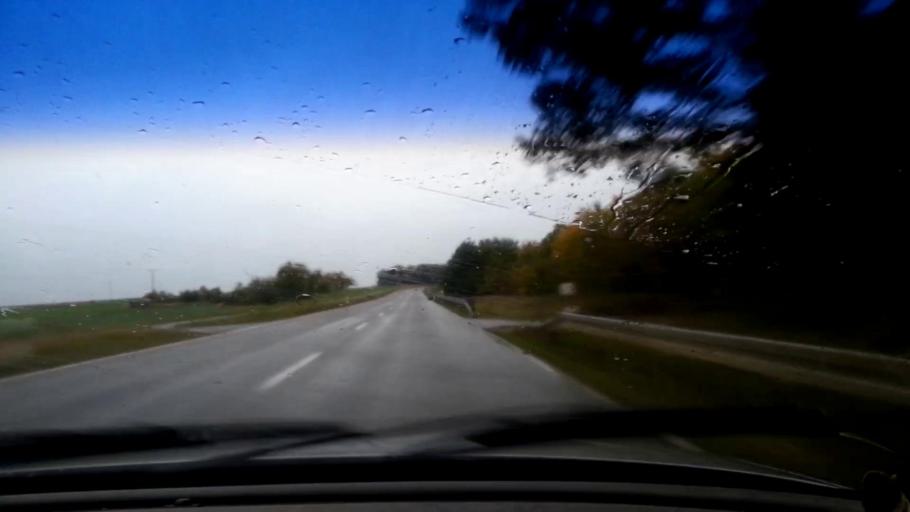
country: DE
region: Bavaria
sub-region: Upper Franconia
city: Walsdorf
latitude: 49.8912
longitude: 10.7787
